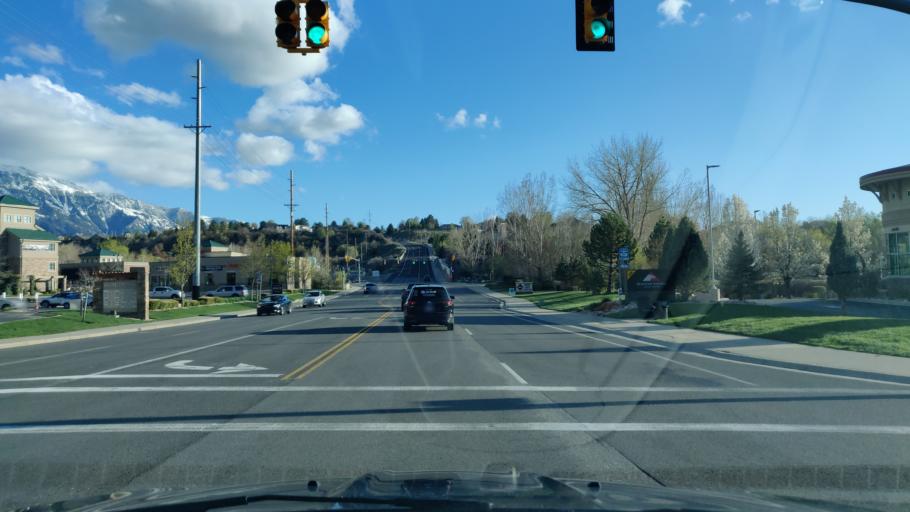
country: US
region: Utah
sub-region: Salt Lake County
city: Cottonwood Heights
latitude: 40.6333
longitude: -111.8065
